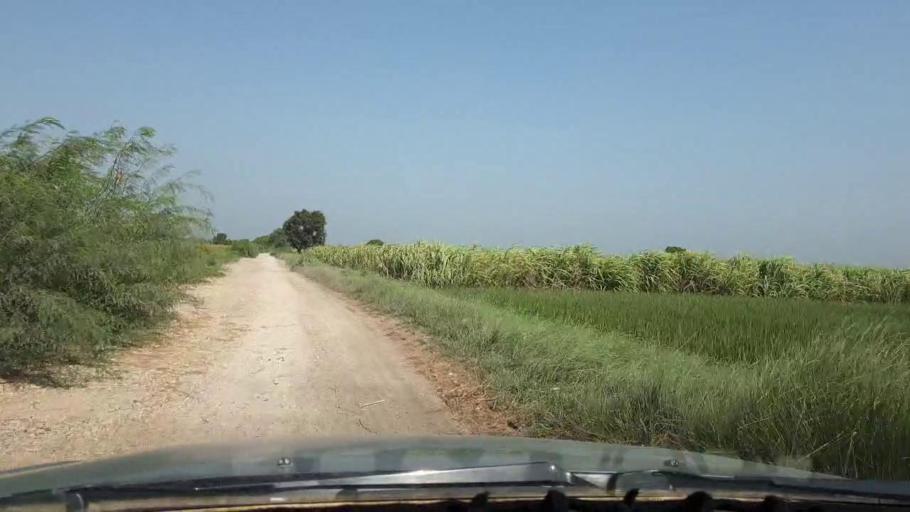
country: PK
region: Sindh
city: Matli
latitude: 25.0842
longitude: 68.6136
